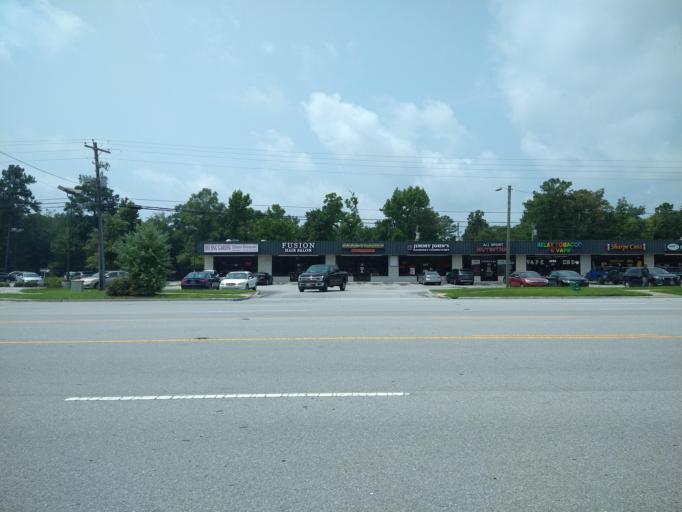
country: US
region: North Carolina
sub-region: Onslow County
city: Pumpkin Center
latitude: 34.7707
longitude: -77.3865
